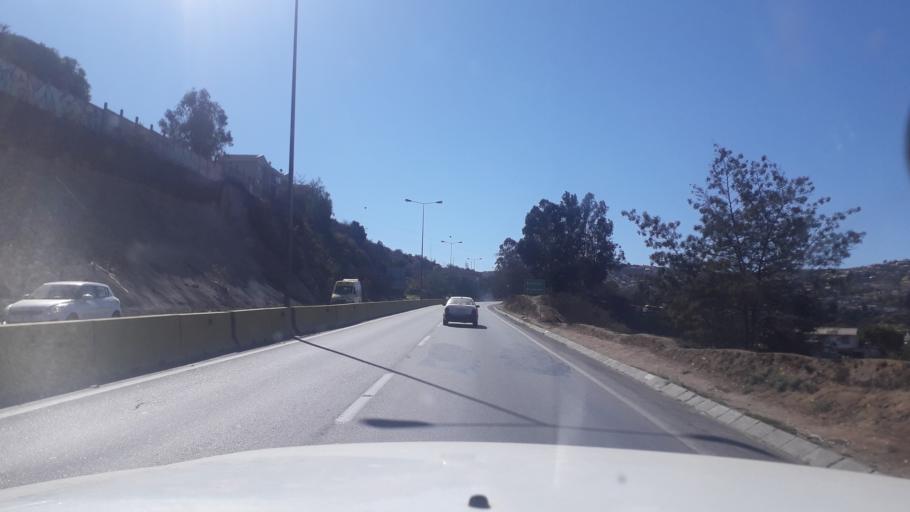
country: CL
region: Valparaiso
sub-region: Provincia de Valparaiso
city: Vina del Mar
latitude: -33.0331
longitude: -71.5009
